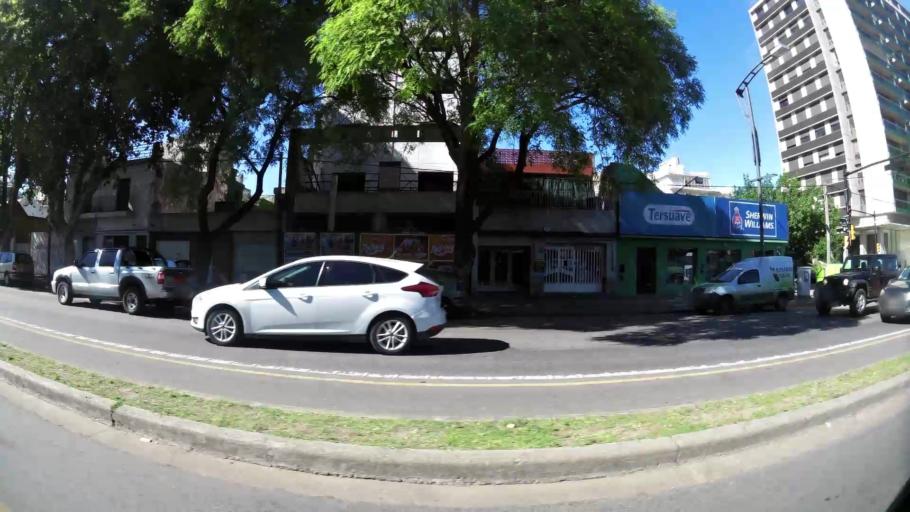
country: AR
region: Santa Fe
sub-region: Departamento de Rosario
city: Rosario
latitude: -32.9511
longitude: -60.6763
